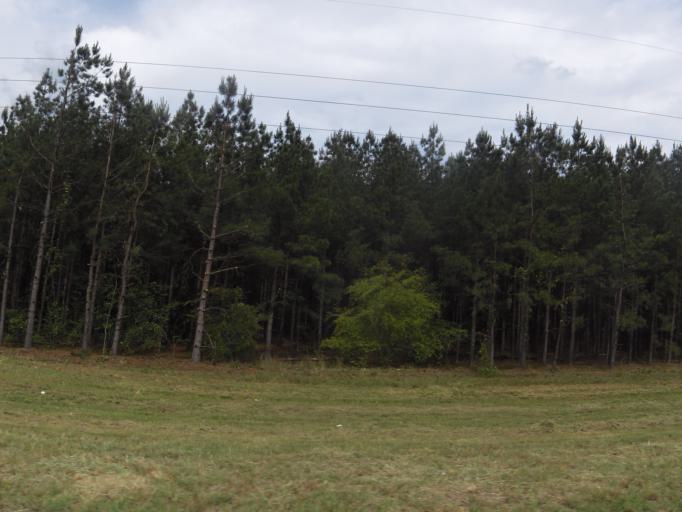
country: US
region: Georgia
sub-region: Jefferson County
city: Louisville
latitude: 33.0919
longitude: -82.4048
